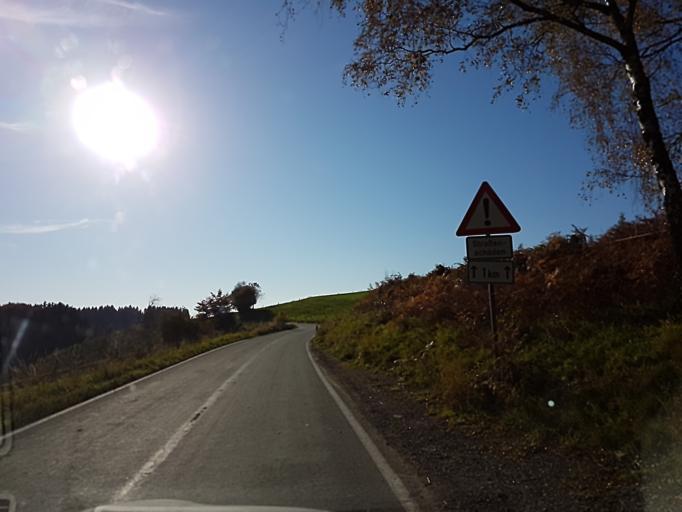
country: DE
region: North Rhine-Westphalia
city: Kierspe
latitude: 51.0764
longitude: 7.5932
